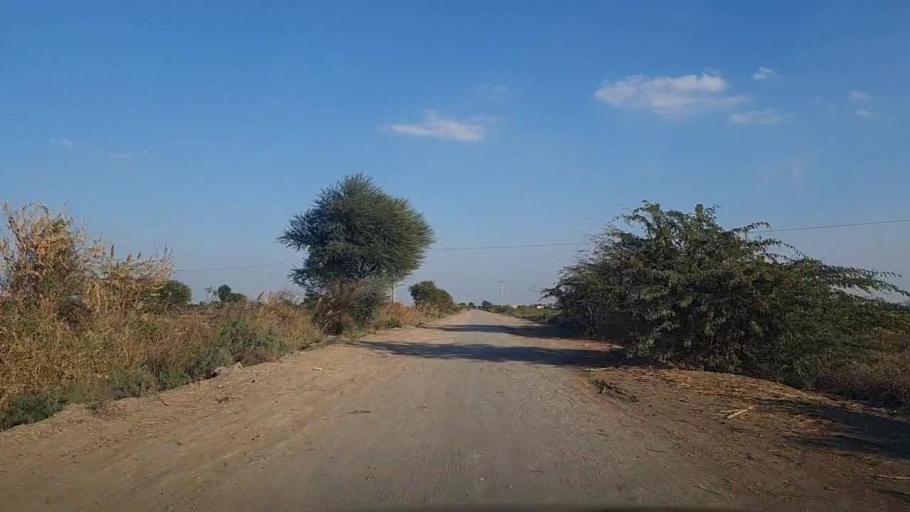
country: PK
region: Sindh
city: Jhol
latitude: 25.9255
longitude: 69.0178
